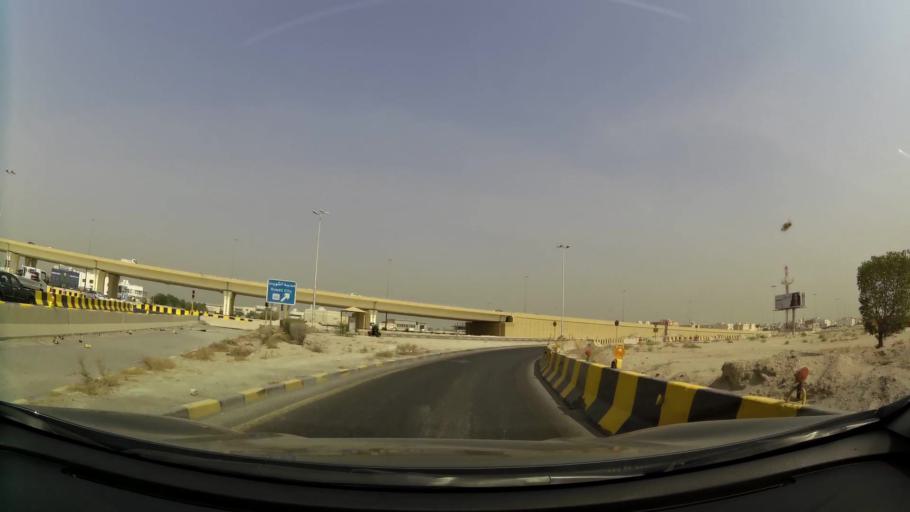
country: KW
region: Al Asimah
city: Ar Rabiyah
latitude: 29.3092
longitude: 47.8658
